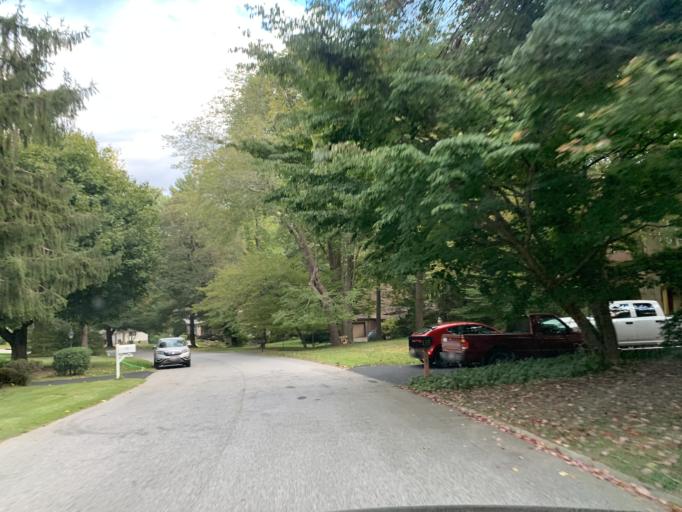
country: US
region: Maryland
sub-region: Harford County
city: Bel Air South
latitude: 39.5142
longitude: -76.3236
